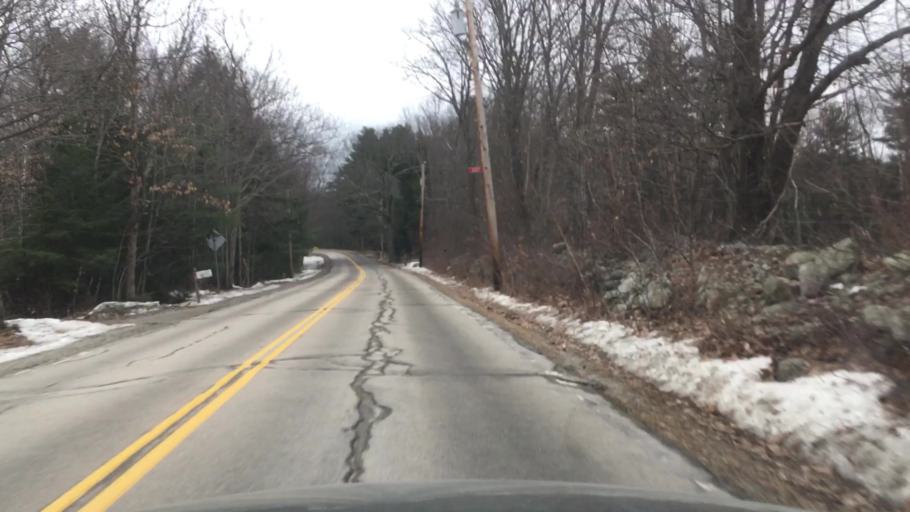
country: US
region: New Hampshire
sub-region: Hillsborough County
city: Mont Vernon
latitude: 42.9418
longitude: -71.6149
